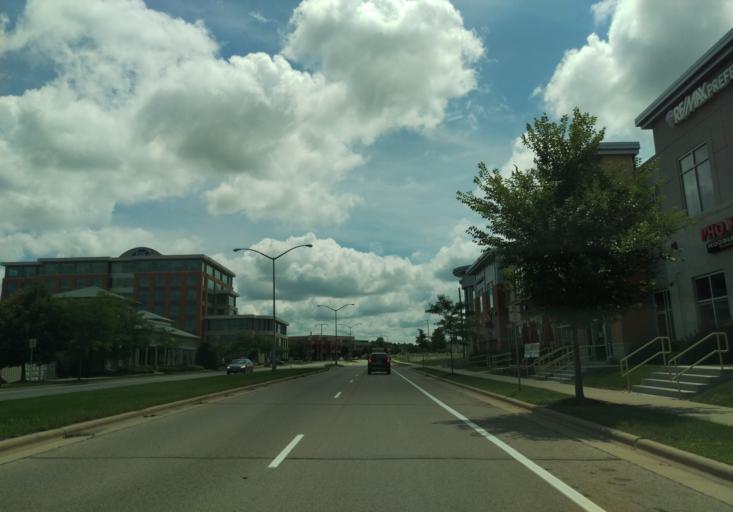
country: US
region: Wisconsin
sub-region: Dane County
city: Middleton
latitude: 43.0737
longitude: -89.5267
